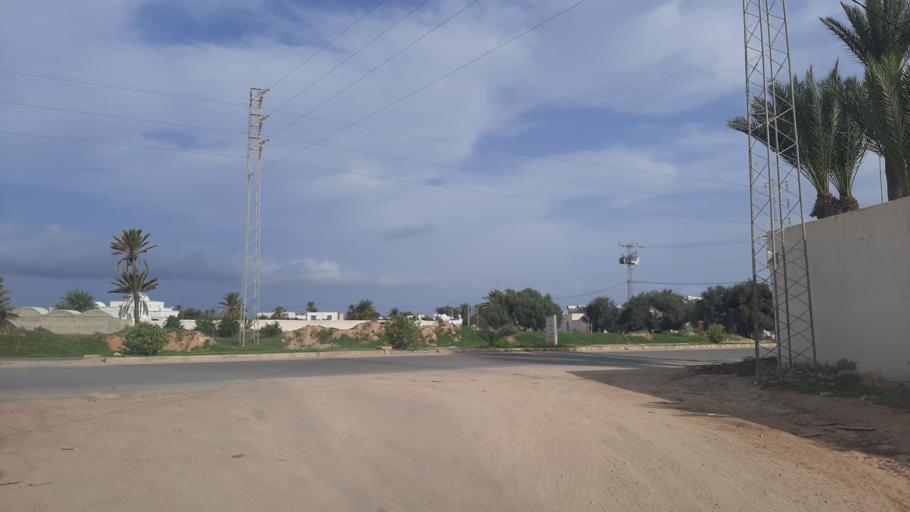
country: TN
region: Madanin
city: Midoun
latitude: 33.8179
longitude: 11.0261
